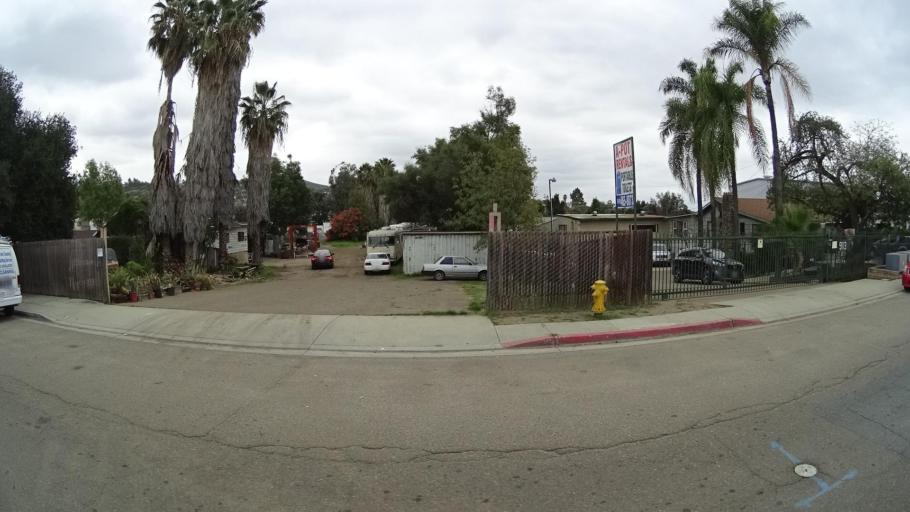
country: US
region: California
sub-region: San Diego County
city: Spring Valley
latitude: 32.7420
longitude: -117.0020
